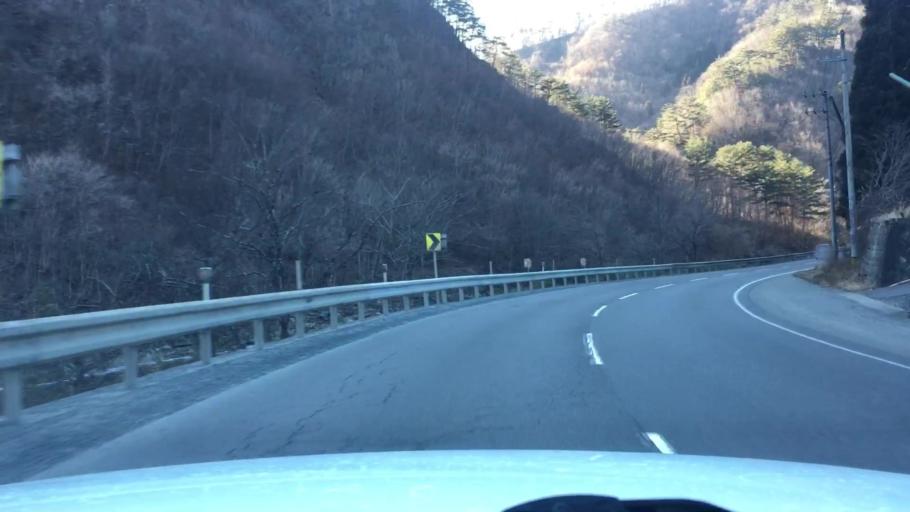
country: JP
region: Iwate
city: Miyako
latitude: 39.6065
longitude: 141.7867
